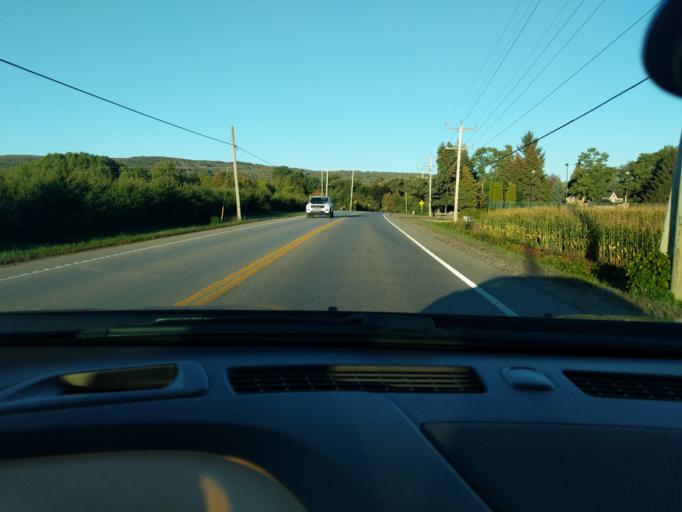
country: CA
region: Ontario
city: Collingwood
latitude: 44.4983
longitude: -80.2738
